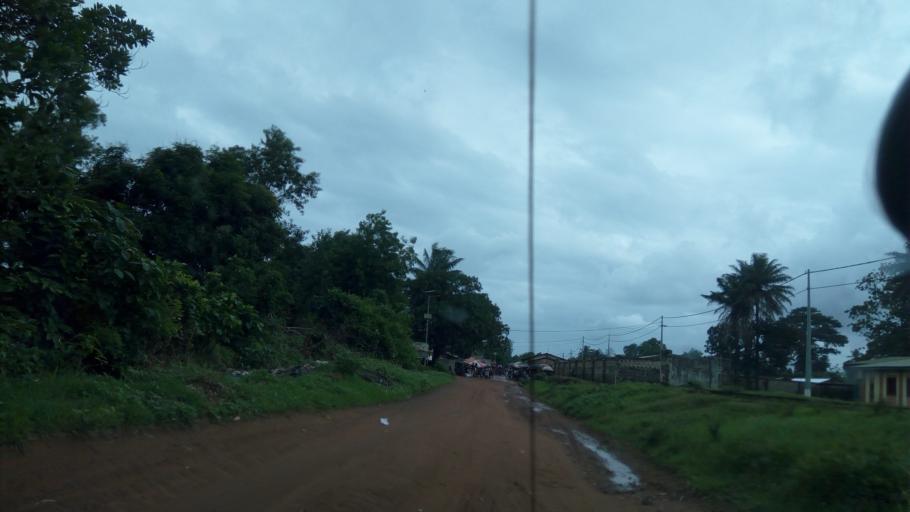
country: SL
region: Northern Province
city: Tintafor
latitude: 8.6266
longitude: -13.2163
